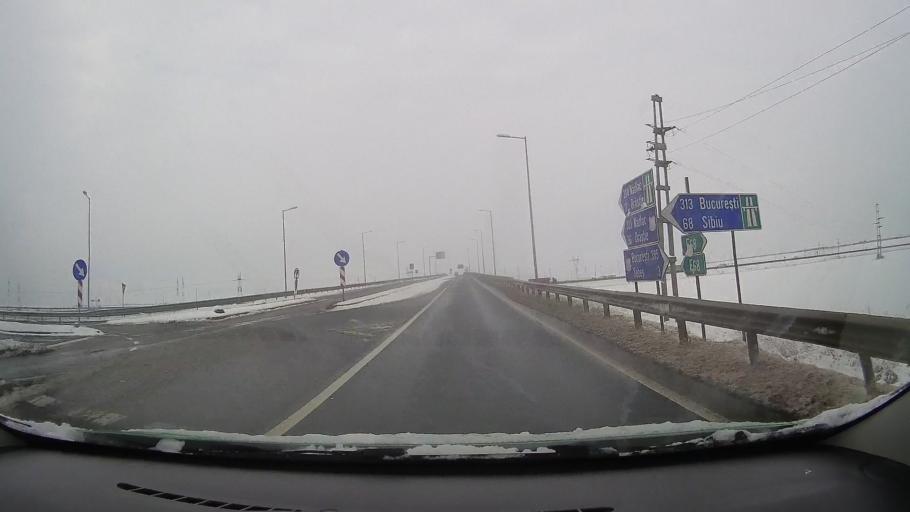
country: RO
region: Alba
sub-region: Municipiul Sebes
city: Lancram
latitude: 45.9750
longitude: 23.5233
